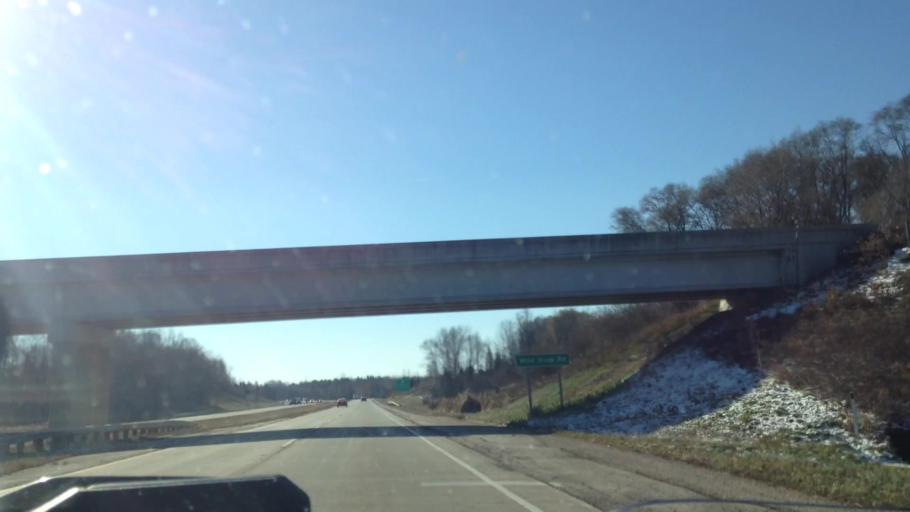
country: US
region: Wisconsin
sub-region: Washington County
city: West Bend
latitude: 43.3767
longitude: -88.1938
